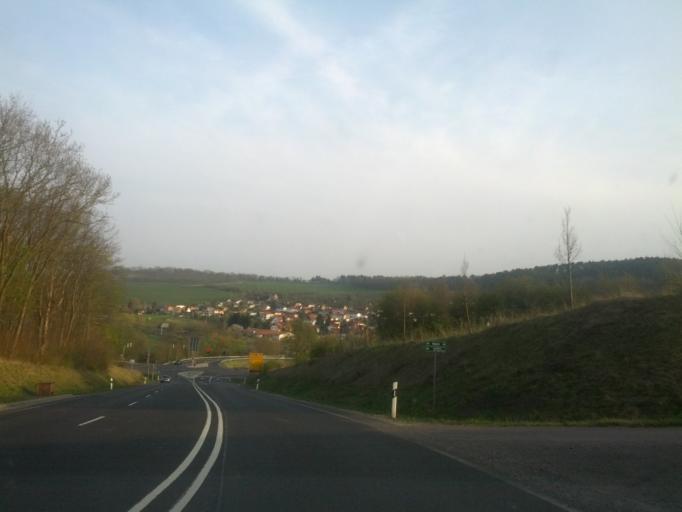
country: DE
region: Thuringia
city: Eisenach
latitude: 50.9824
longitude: 10.3588
